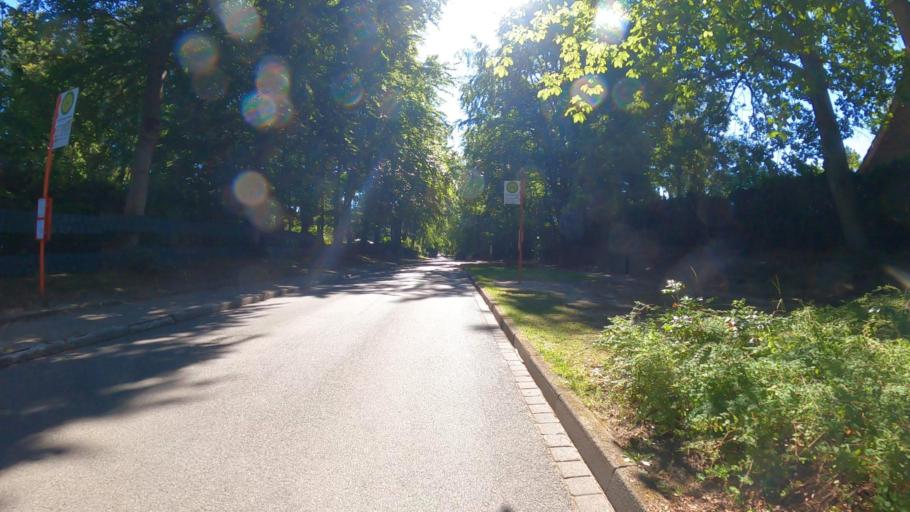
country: DE
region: Schleswig-Holstein
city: Aumuhle
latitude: 53.5234
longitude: 10.3189
